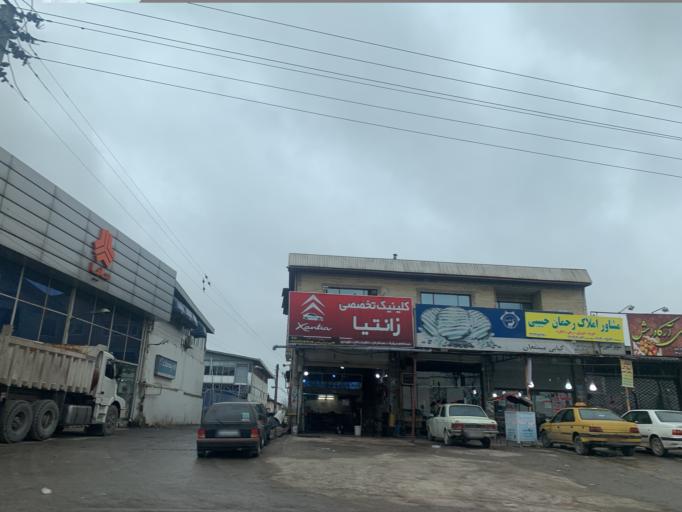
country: IR
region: Mazandaran
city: Amol
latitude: 36.4261
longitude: 52.3498
